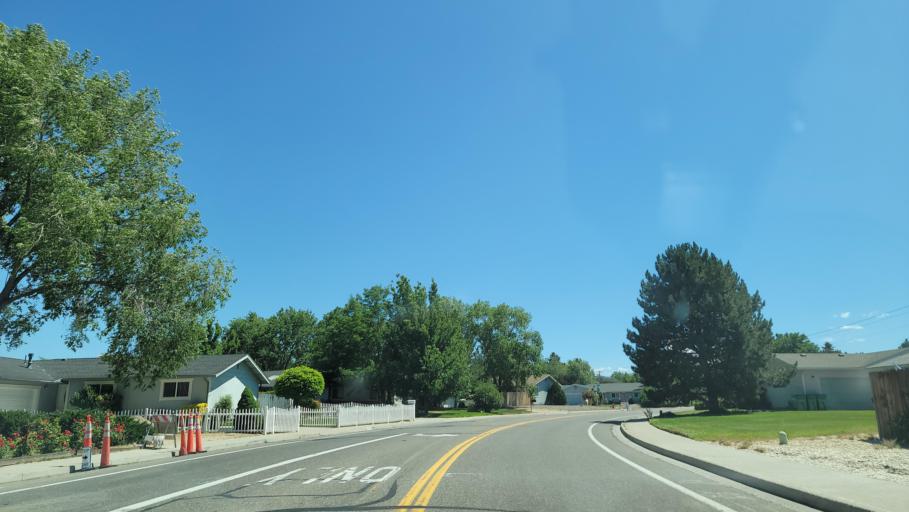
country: US
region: Nevada
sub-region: Carson City
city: Carson City
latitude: 39.1464
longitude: -119.7628
